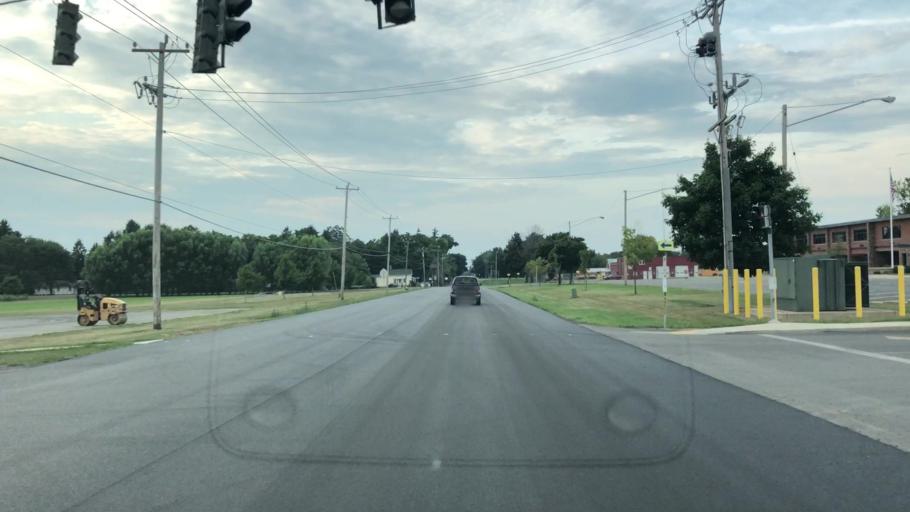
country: US
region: New York
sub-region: Erie County
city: Elma Center
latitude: 42.8352
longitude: -78.6060
